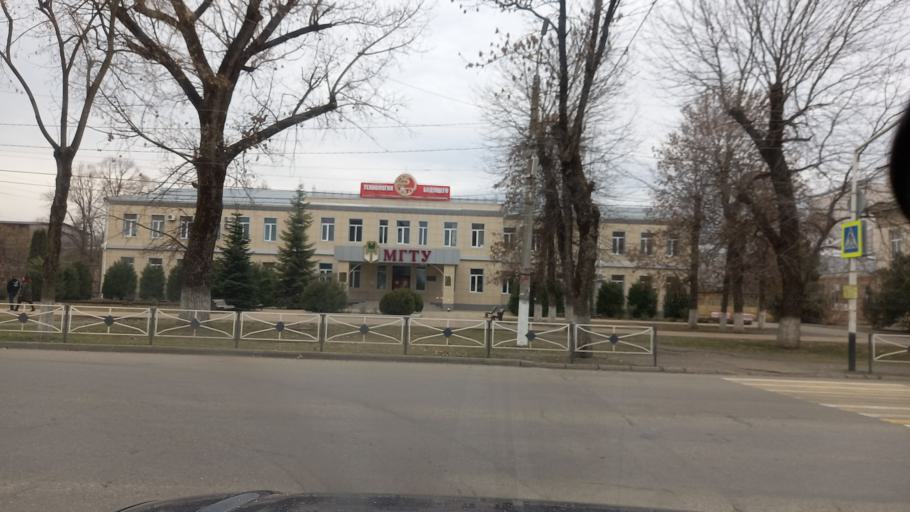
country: RU
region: Adygeya
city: Maykop
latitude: 44.6011
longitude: 40.1055
